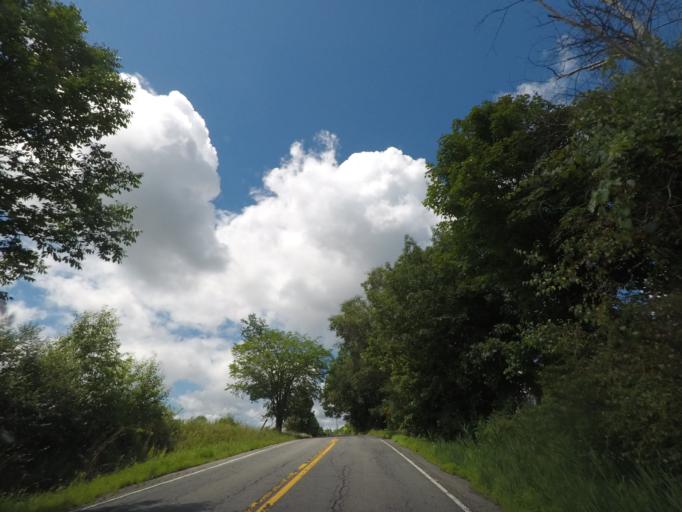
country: US
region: New York
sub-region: Rensselaer County
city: Wynantskill
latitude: 42.6705
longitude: -73.6644
